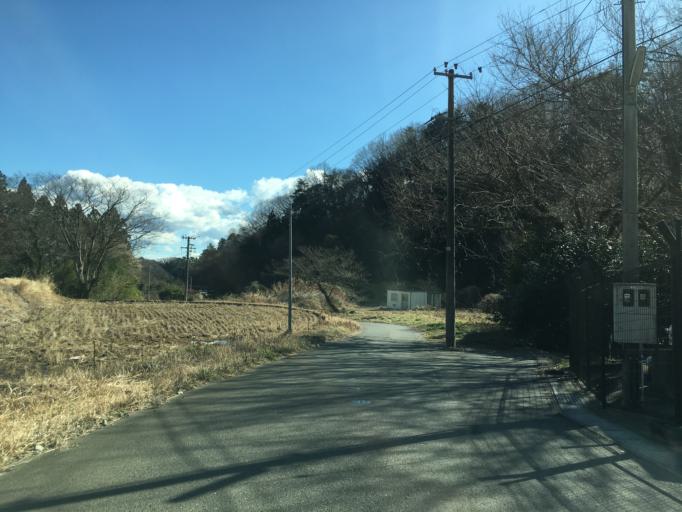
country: JP
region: Fukushima
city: Iwaki
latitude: 37.0121
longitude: 140.7889
